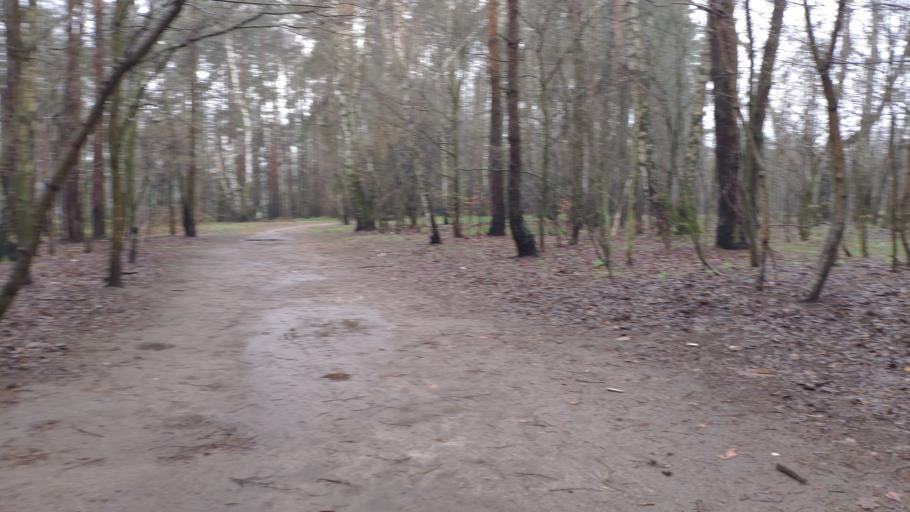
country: PL
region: Lodz Voivodeship
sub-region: Powiat lodzki wschodni
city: Andrespol
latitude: 51.7516
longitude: 19.5693
